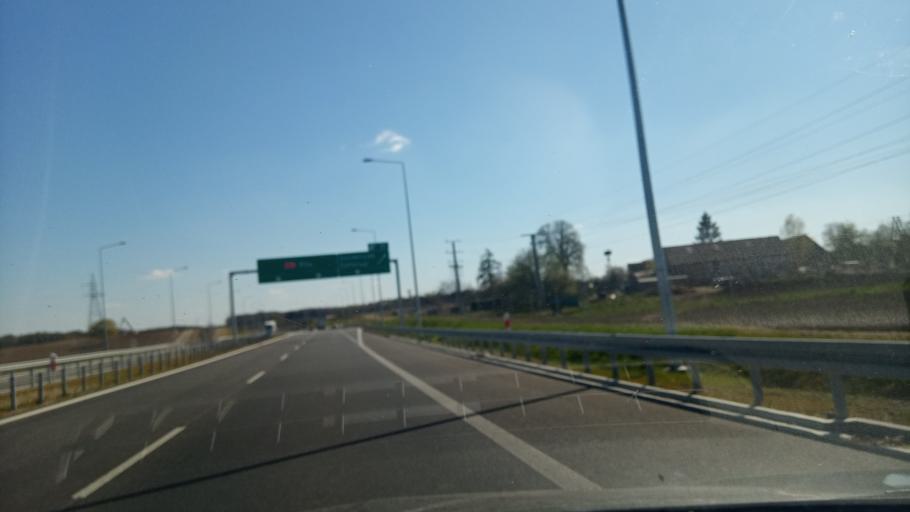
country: PL
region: West Pomeranian Voivodeship
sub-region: Powiat szczecinecki
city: Szczecinek
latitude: 53.6949
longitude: 16.7302
